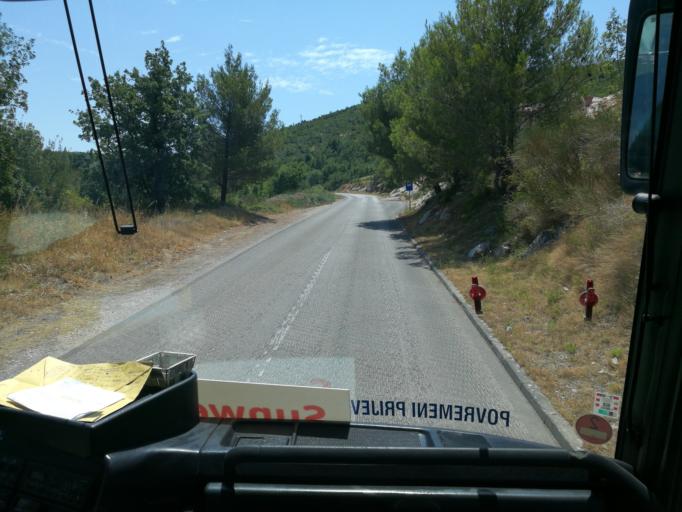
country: HR
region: Dubrovacko-Neretvanska
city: Cavtat
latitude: 42.5795
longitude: 18.2310
